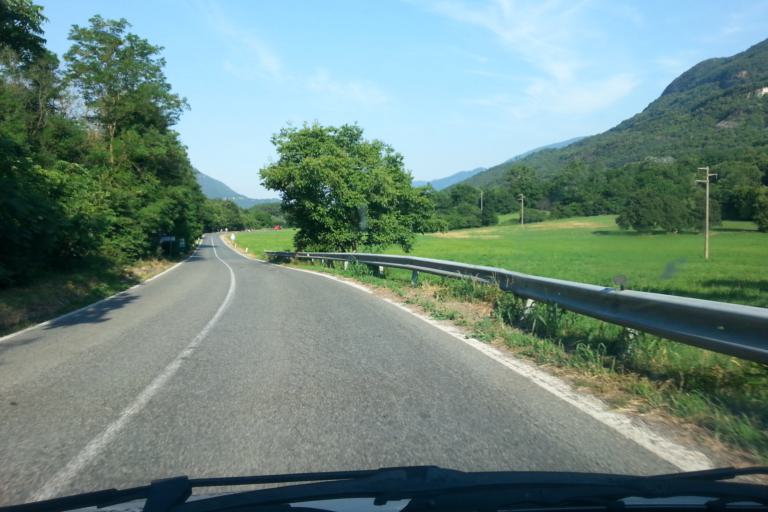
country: IT
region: Piedmont
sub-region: Provincia di Torino
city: San Giorio
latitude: 45.1245
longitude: 7.1852
